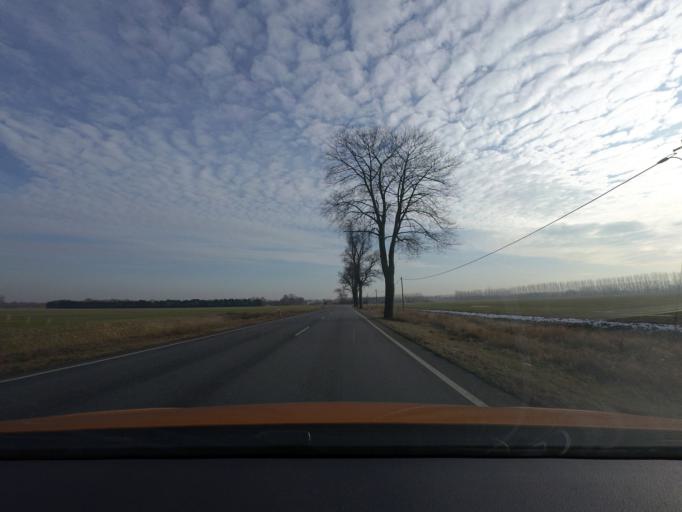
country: DE
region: Brandenburg
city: Liebenwalde
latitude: 52.8849
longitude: 13.3386
